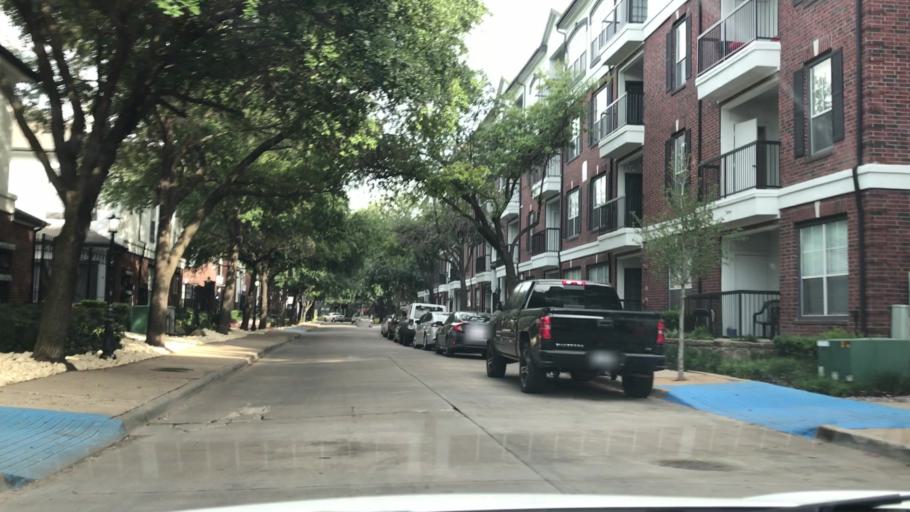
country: US
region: Texas
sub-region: Dallas County
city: Dallas
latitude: 32.7918
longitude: -96.7909
